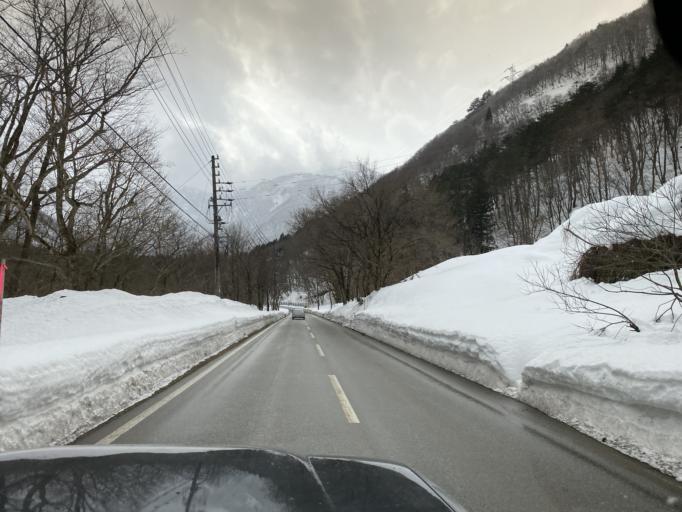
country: JP
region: Toyama
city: Fukumitsu
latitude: 36.2383
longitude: 136.8865
